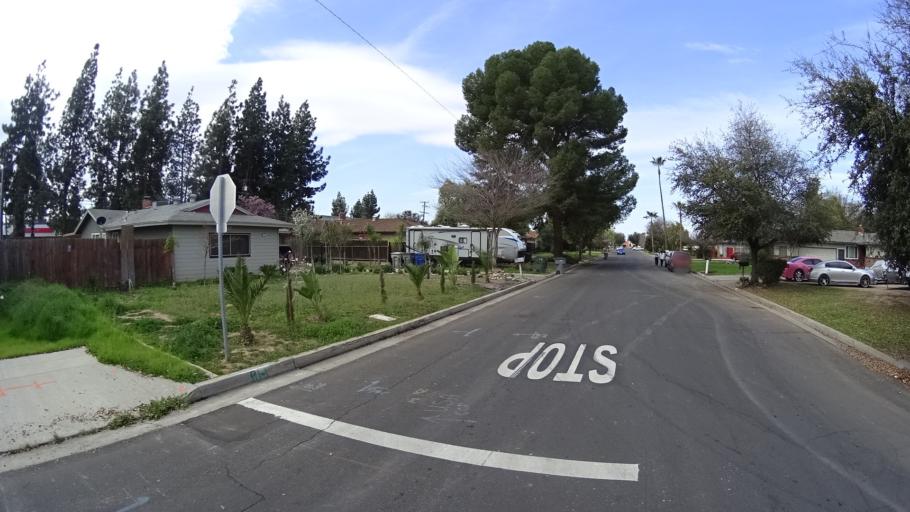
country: US
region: California
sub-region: Fresno County
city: Fresno
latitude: 36.8104
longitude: -119.7768
